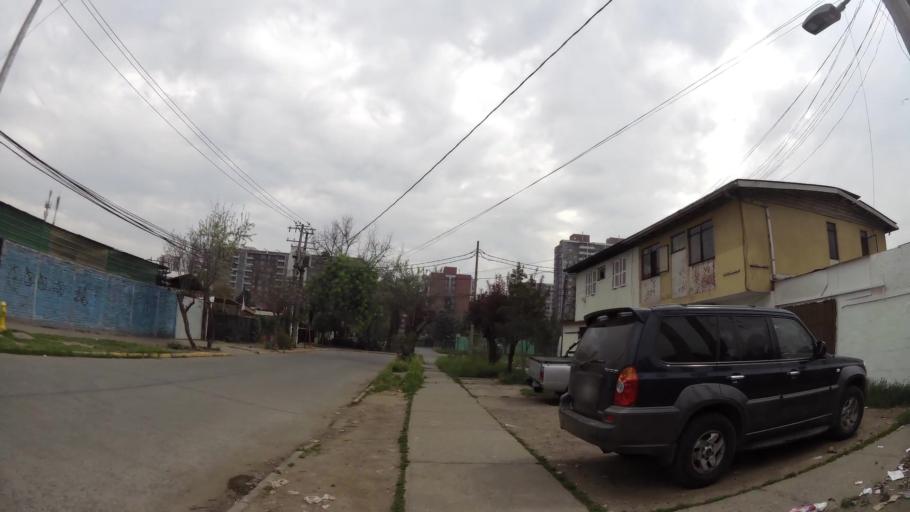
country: CL
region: Santiago Metropolitan
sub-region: Provincia de Santiago
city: Villa Presidente Frei, Nunoa, Santiago, Chile
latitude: -33.4787
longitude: -70.5954
